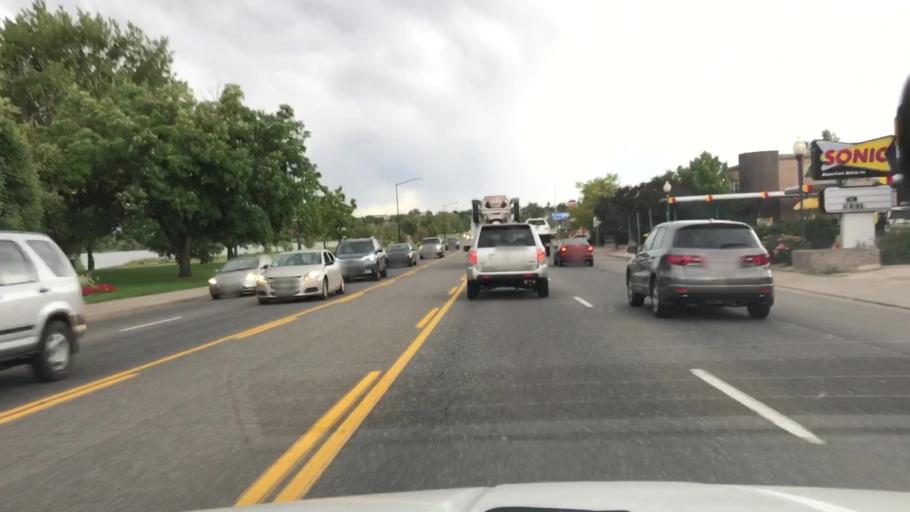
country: US
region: Colorado
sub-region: Jefferson County
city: Edgewater
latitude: 39.7523
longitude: -105.0532
